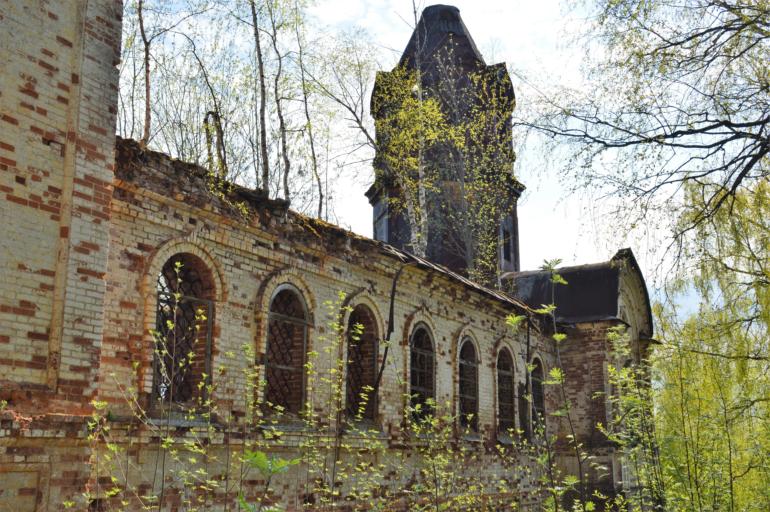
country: RU
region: Kirov
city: Nolinsk
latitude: 57.6973
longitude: 49.9268
